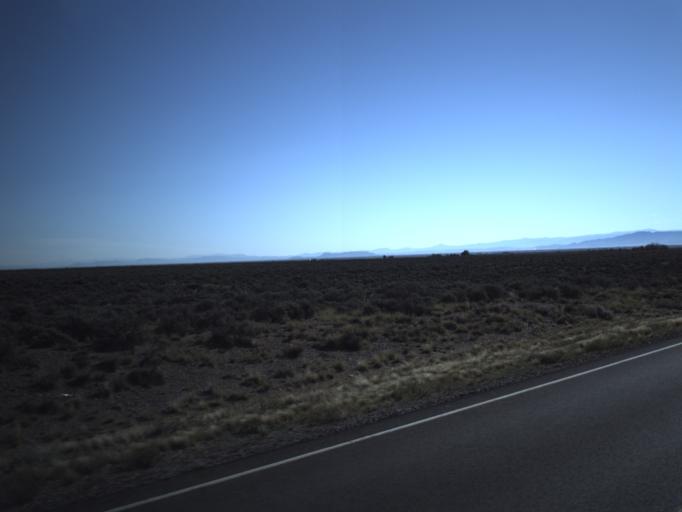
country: US
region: Utah
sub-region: Washington County
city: Enterprise
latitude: 37.7982
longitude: -113.9101
